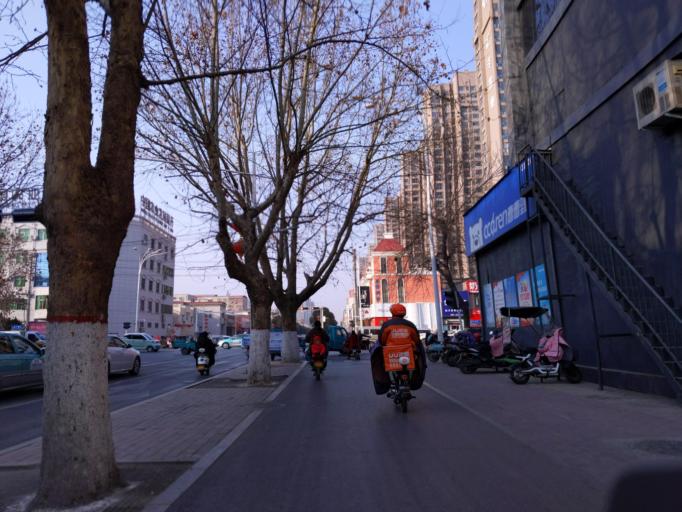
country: CN
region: Henan Sheng
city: Puyang
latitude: 35.7716
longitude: 115.0327
